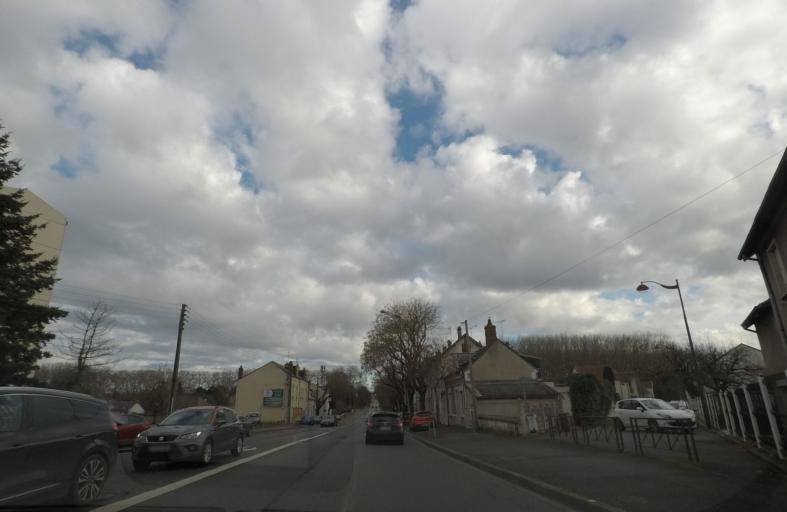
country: FR
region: Centre
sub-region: Departement du Cher
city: Bourges
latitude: 47.0714
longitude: 2.3888
